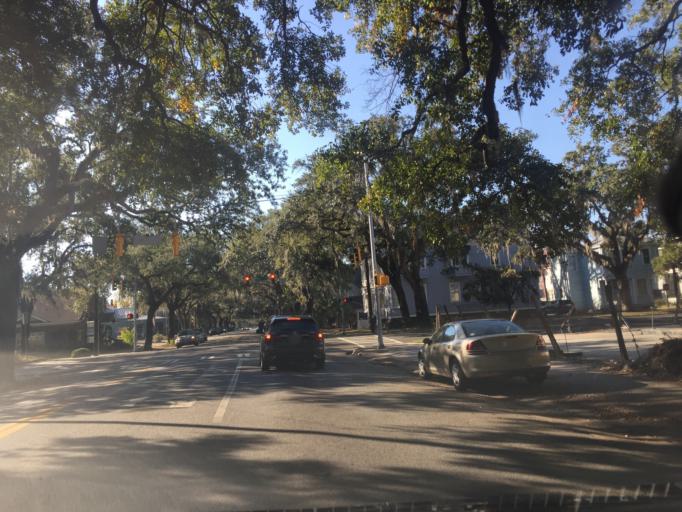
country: US
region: Georgia
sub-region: Chatham County
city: Savannah
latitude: 32.0576
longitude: -81.1001
